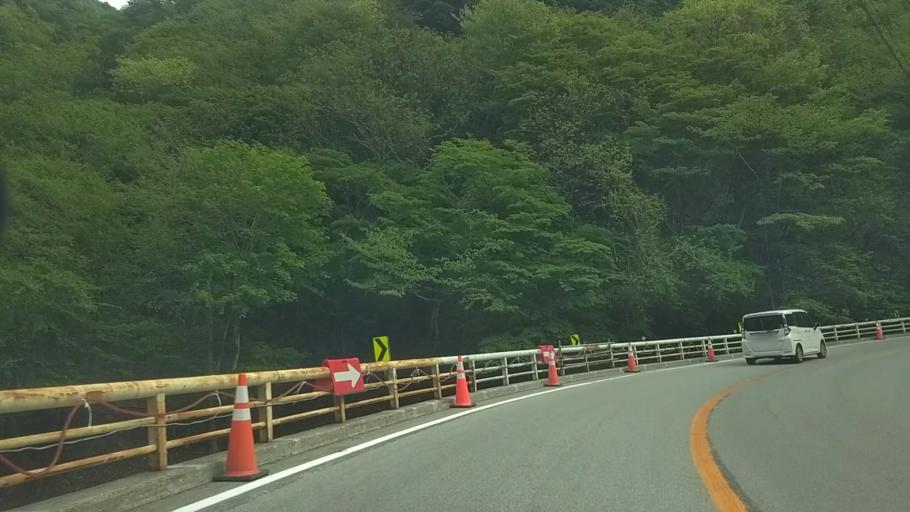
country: JP
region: Yamanashi
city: Fujikawaguchiko
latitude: 35.5087
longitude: 138.6167
